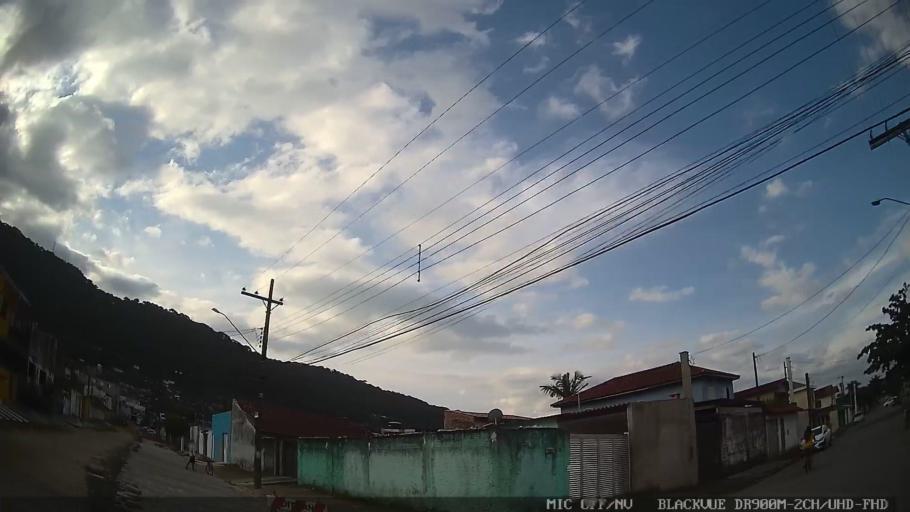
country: BR
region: Sao Paulo
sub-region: Guaruja
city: Guaruja
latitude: -23.9805
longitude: -46.2374
